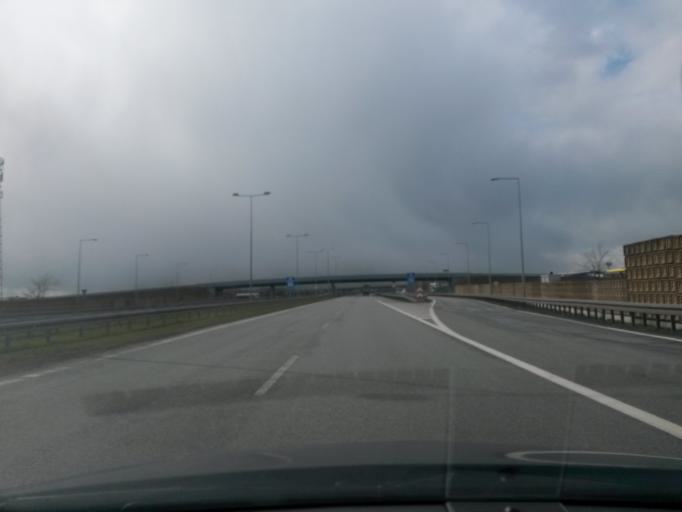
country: PL
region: Greater Poland Voivodeship
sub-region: Powiat koninski
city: Stare Miasto
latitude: 52.1622
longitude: 18.2149
